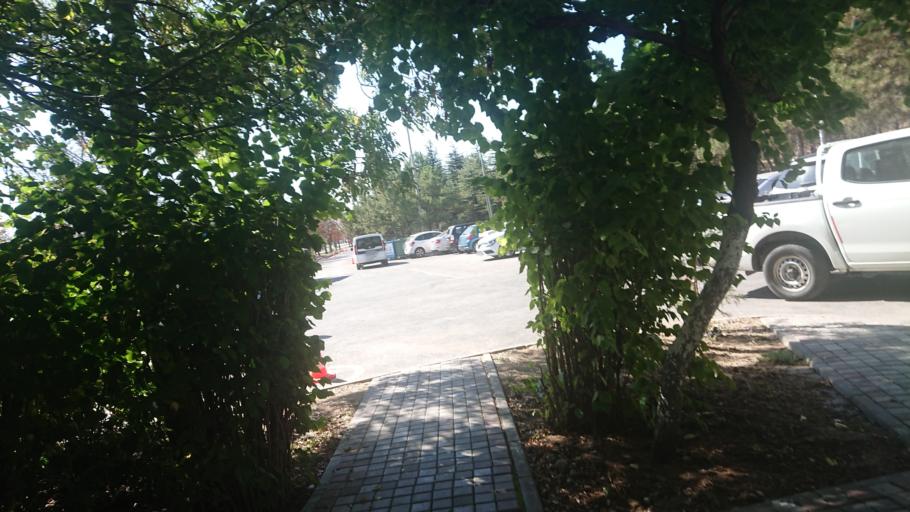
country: TR
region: Ankara
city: Ankara
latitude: 39.9077
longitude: 32.7840
